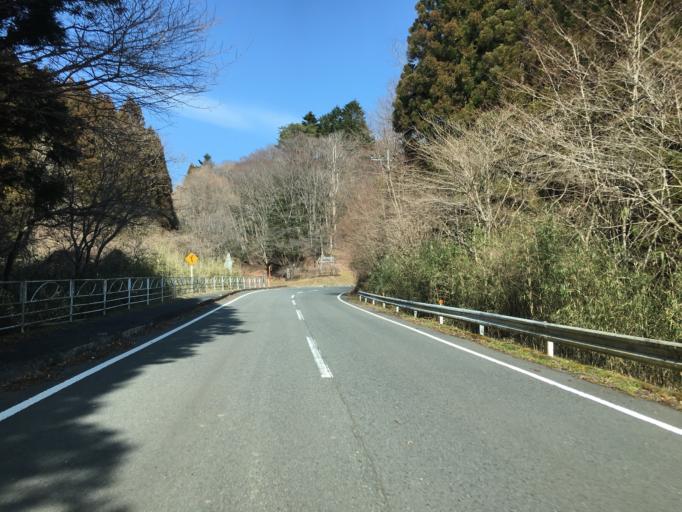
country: JP
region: Ibaraki
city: Takahagi
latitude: 36.7975
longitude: 140.5840
